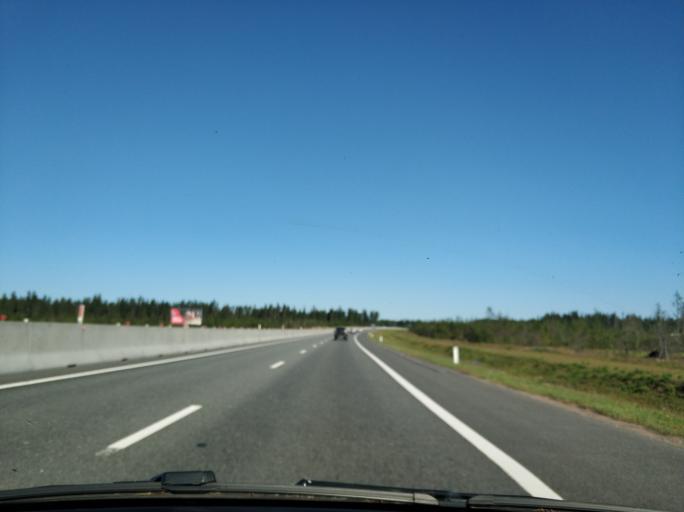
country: RU
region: Leningrad
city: Sosnovo
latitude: 60.4392
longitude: 30.2168
